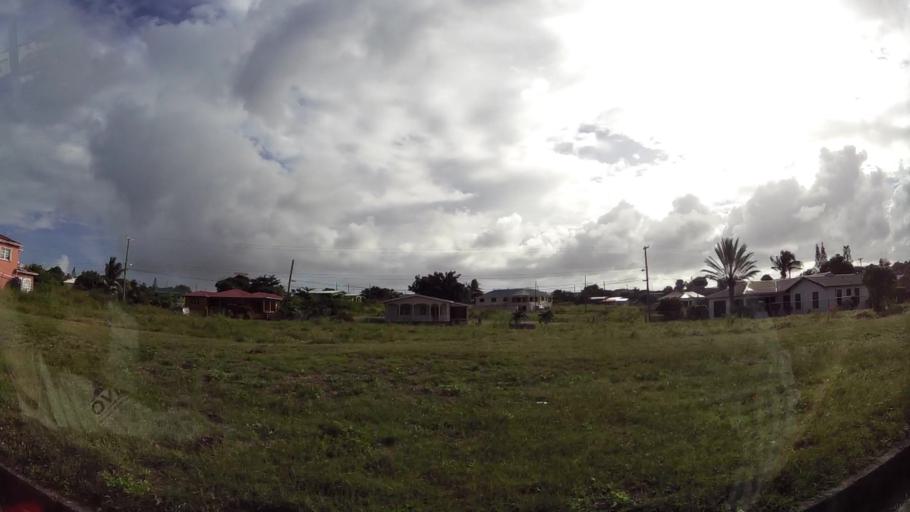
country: AG
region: Saint John
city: Saint John's
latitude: 17.1293
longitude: -61.8324
